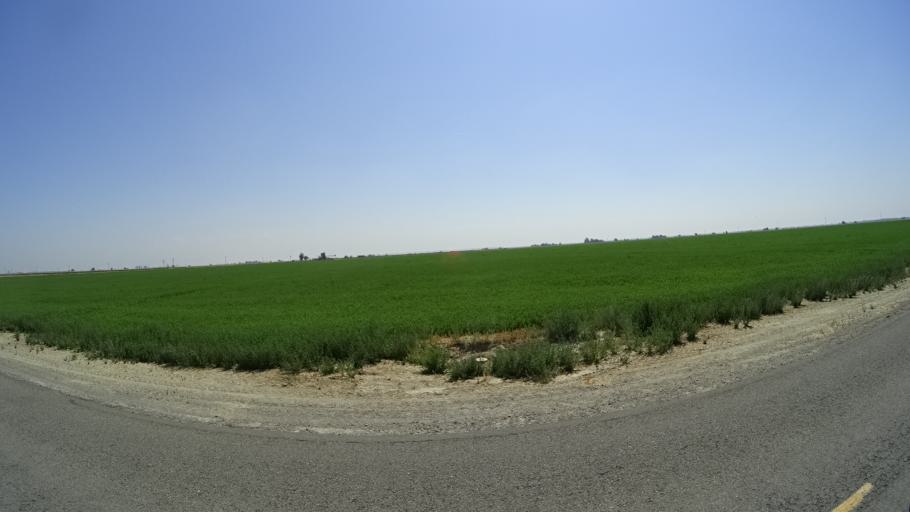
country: US
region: California
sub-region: Tulare County
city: Goshen
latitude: 36.3769
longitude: -119.5290
